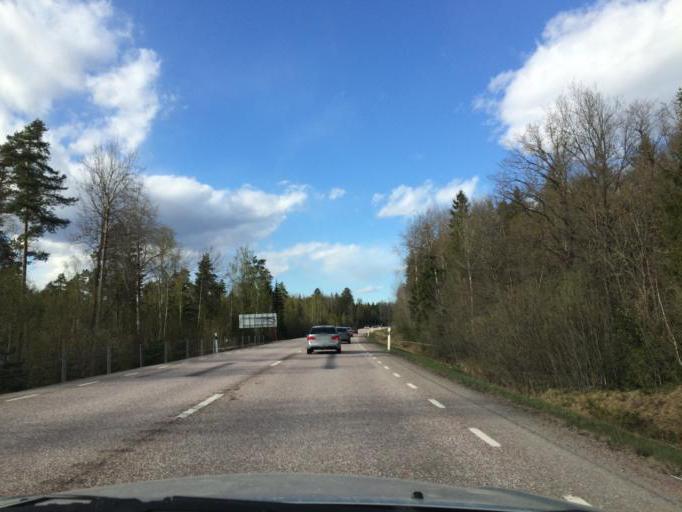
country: SE
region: Soedermanland
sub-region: Eskilstuna Kommun
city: Kvicksund
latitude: 59.4993
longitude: 16.3037
